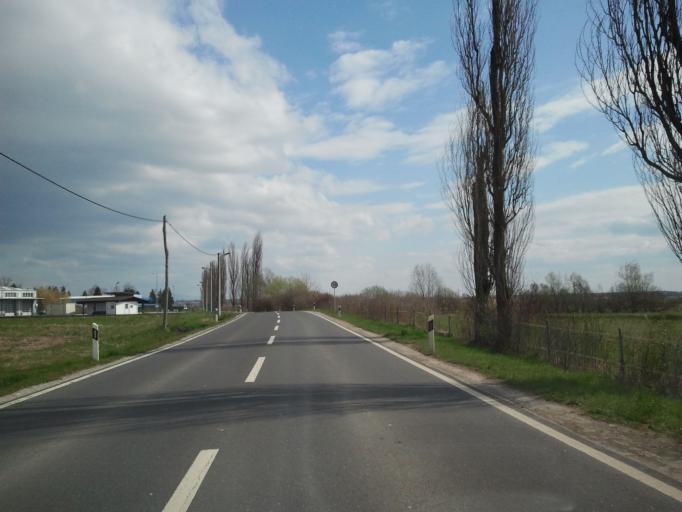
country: HR
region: Zagrebacka
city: Jastrebarsko
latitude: 45.6480
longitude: 15.6249
